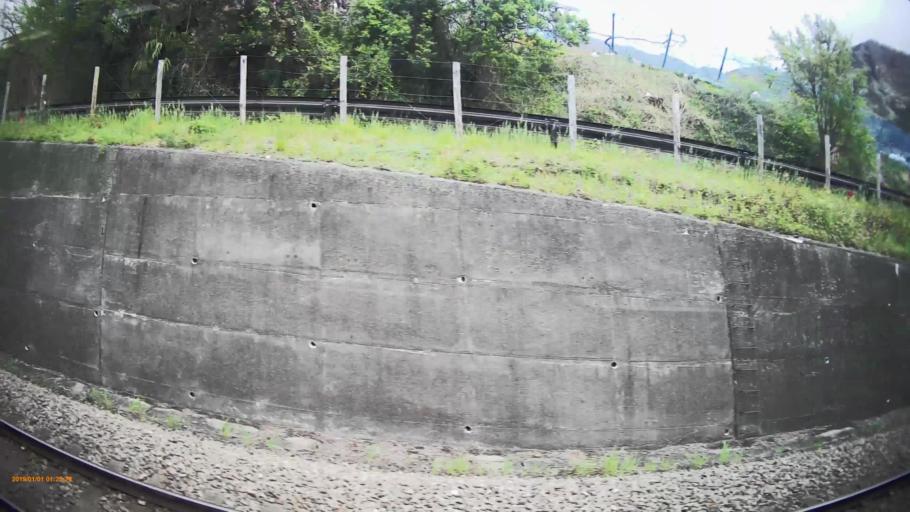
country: JP
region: Yamanashi
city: Enzan
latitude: 35.6767
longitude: 138.7429
